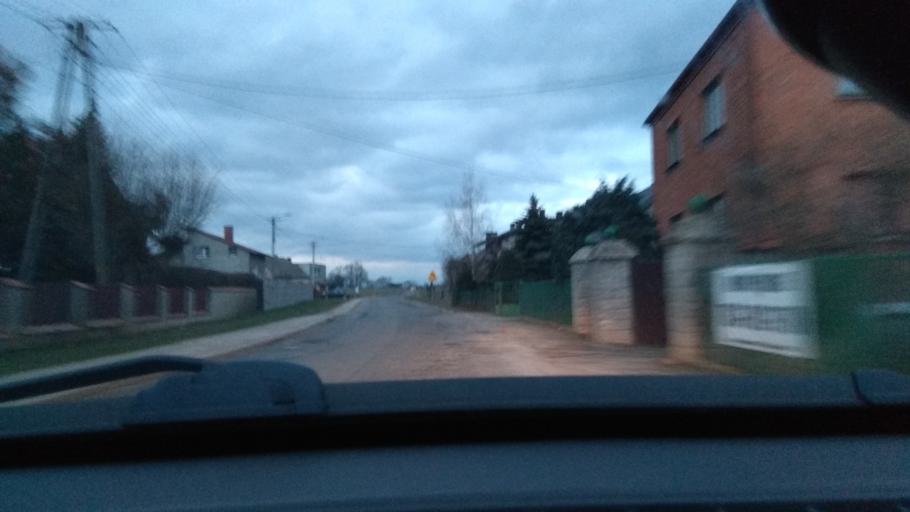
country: PL
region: Lodz Voivodeship
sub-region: Powiat wieruszowski
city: Wieruszow
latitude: 51.3070
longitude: 18.0817
